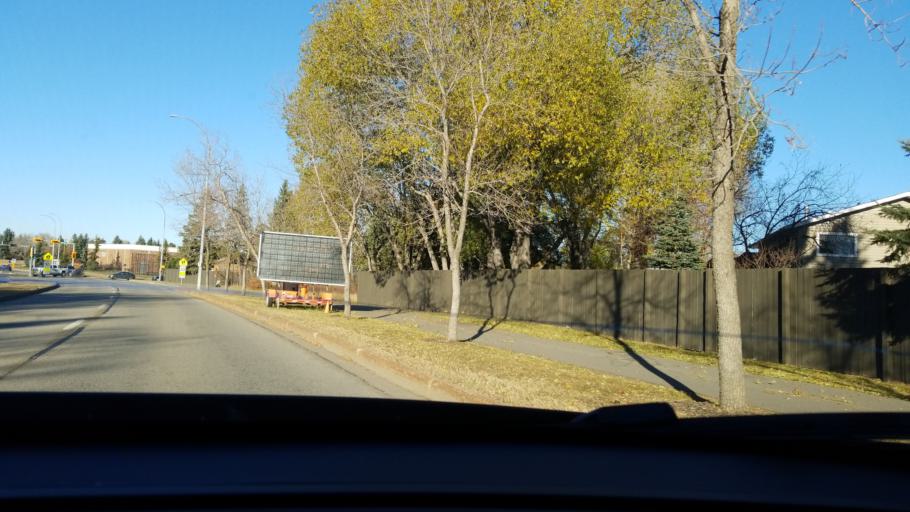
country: CA
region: Alberta
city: Sherwood Park
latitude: 53.5285
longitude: -113.2808
